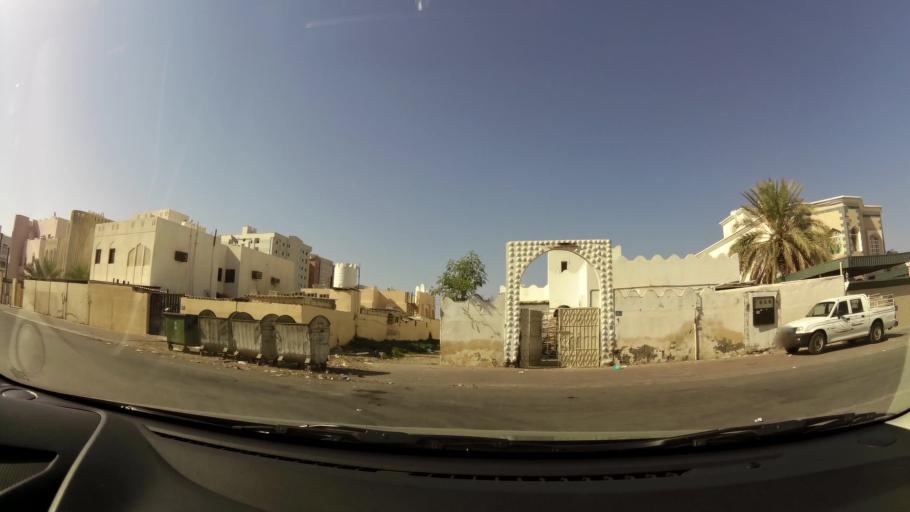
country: OM
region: Muhafazat Masqat
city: As Sib al Jadidah
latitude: 23.6303
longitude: 58.1993
